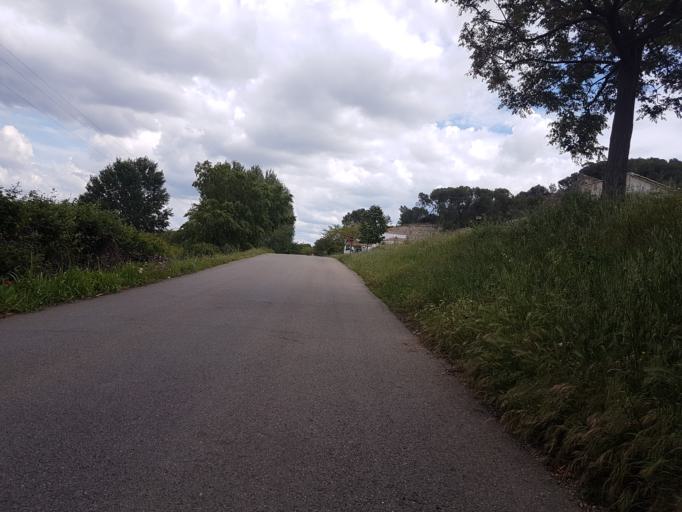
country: FR
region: Languedoc-Roussillon
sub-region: Departement du Gard
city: Beaucaire
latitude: 43.8192
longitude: 4.6341
